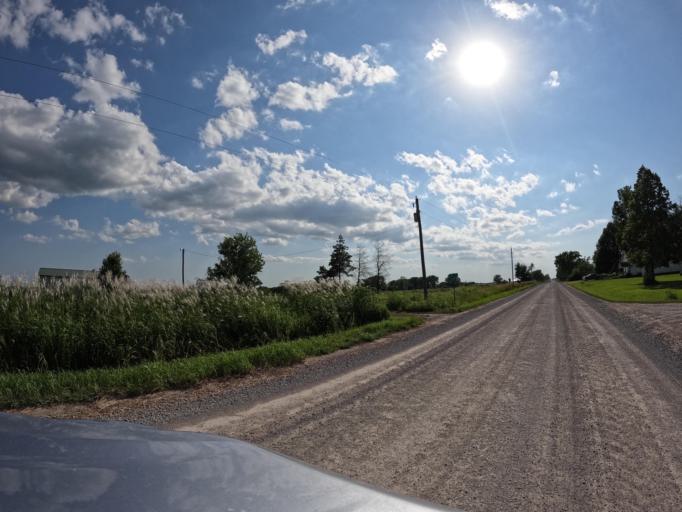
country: US
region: Iowa
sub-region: Appanoose County
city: Centerville
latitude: 40.7178
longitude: -93.0318
